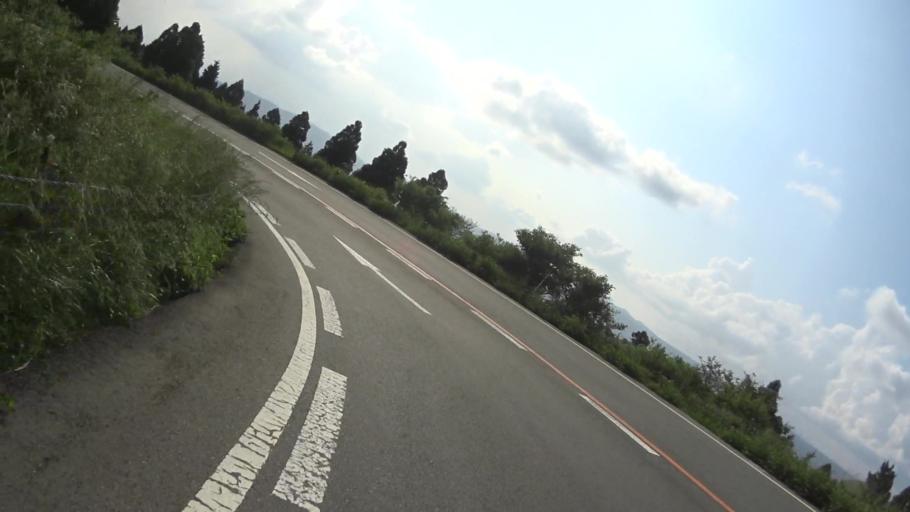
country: JP
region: Kumamoto
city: Aso
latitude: 32.8986
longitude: 131.0464
